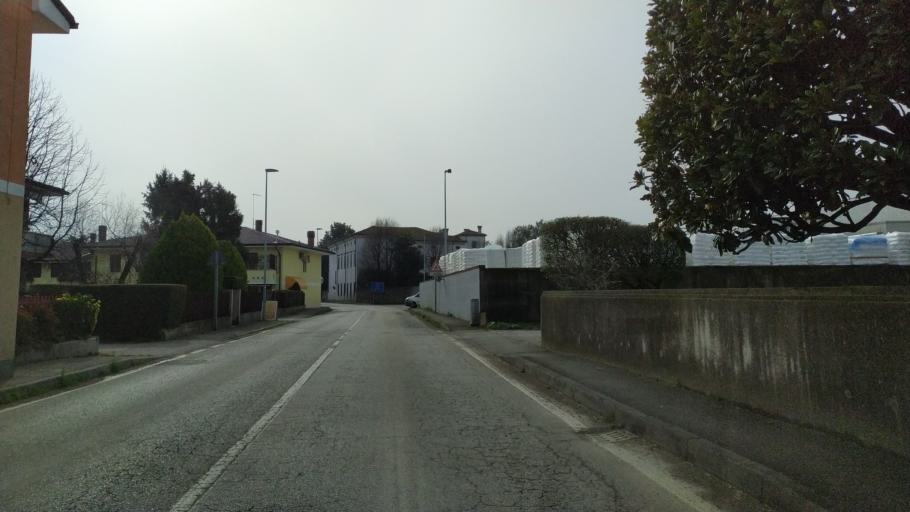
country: IT
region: Veneto
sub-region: Provincia di Padova
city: San Pietro in Gu
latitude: 45.6213
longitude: 11.6734
